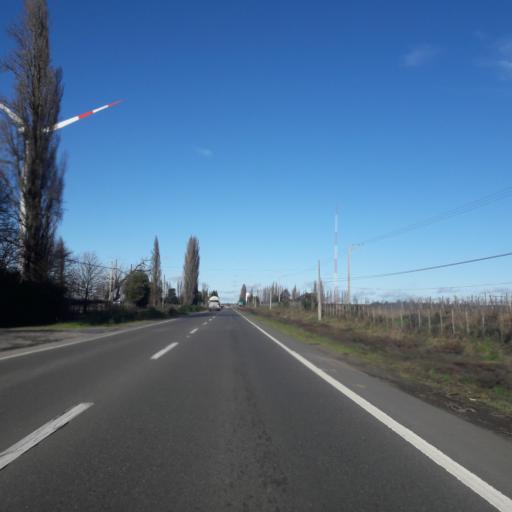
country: CL
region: Araucania
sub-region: Provincia de Malleco
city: Angol
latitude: -37.7132
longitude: -72.6052
